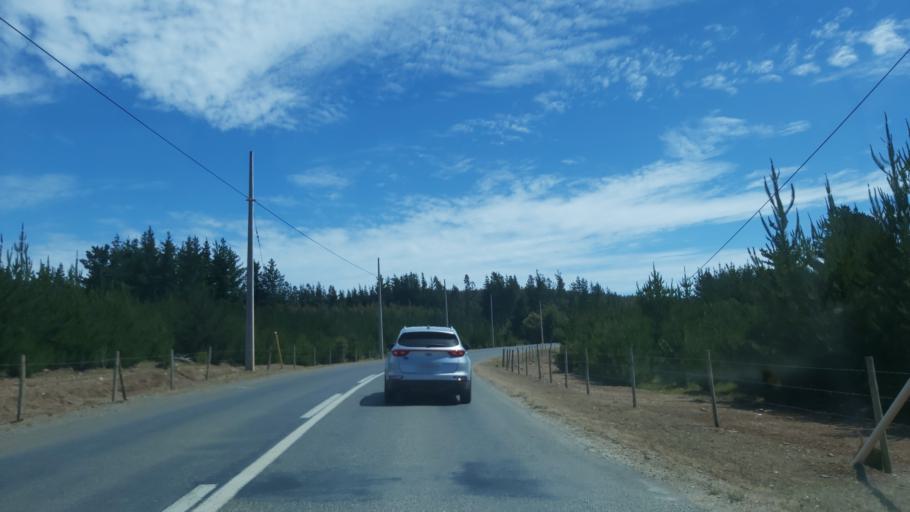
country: CL
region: Maule
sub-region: Provincia de Talca
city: Constitucion
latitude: -35.5366
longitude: -72.5462
